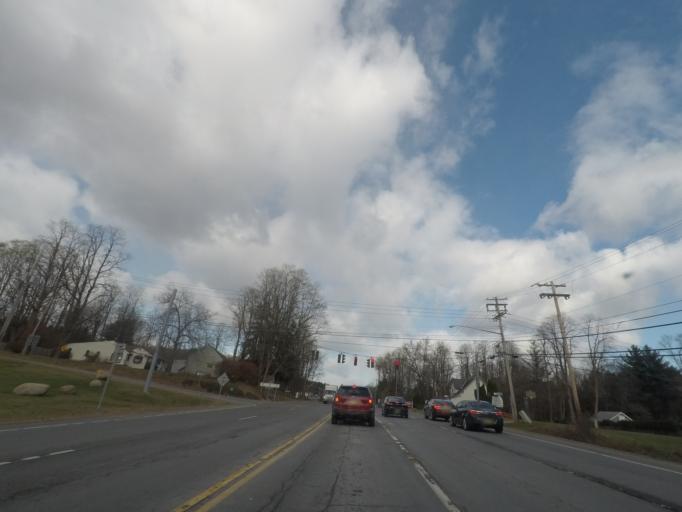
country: US
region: New York
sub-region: Saratoga County
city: Ballston Spa
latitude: 43.0110
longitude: -73.7897
